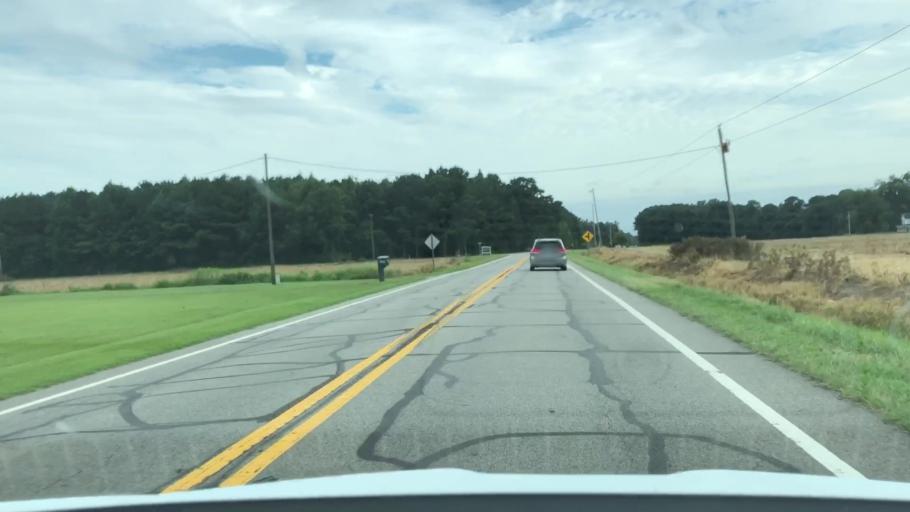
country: US
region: North Carolina
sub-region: Lenoir County
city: Kinston
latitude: 35.1612
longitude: -77.5555
